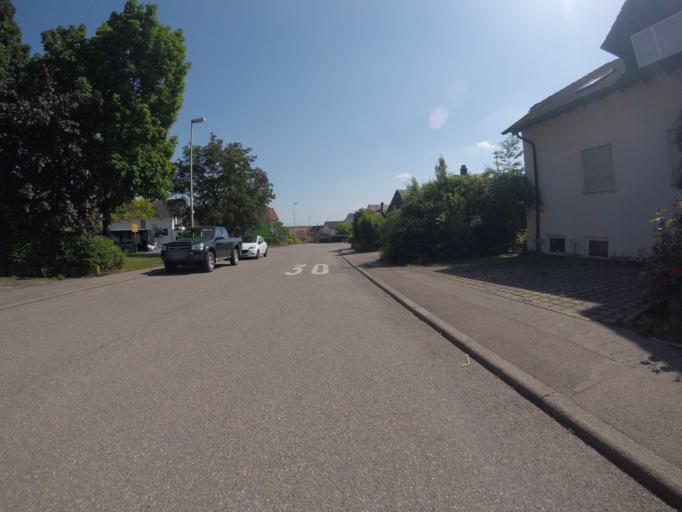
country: DE
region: Baden-Wuerttemberg
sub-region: Regierungsbezirk Stuttgart
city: Kirchberg an der Murr
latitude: 48.9640
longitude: 9.3289
